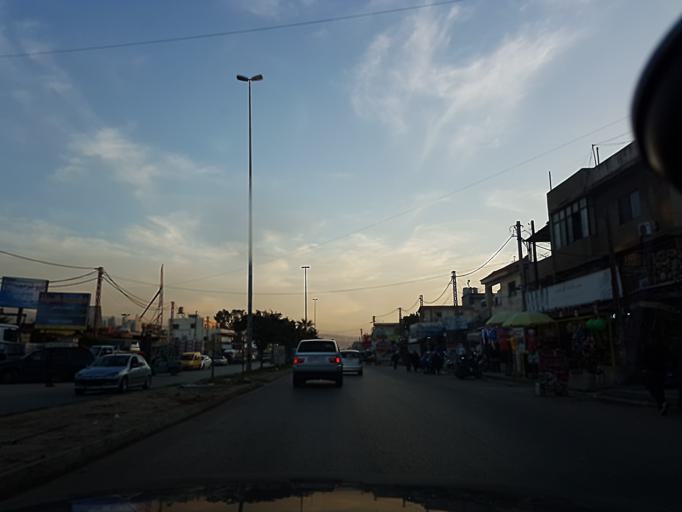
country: LB
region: Beyrouth
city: Beirut
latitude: 33.8332
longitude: 35.4845
